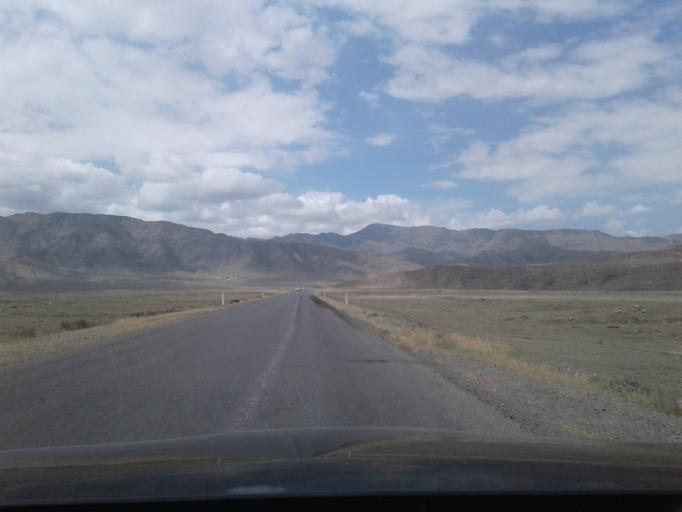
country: TM
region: Ahal
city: Baharly
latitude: 38.5179
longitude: 57.1370
